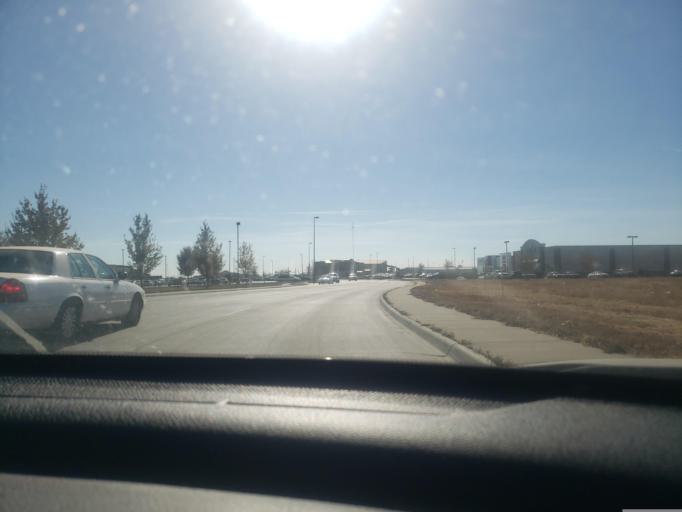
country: US
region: Kansas
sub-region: Finney County
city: Garden City
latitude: 37.9782
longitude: -100.8367
